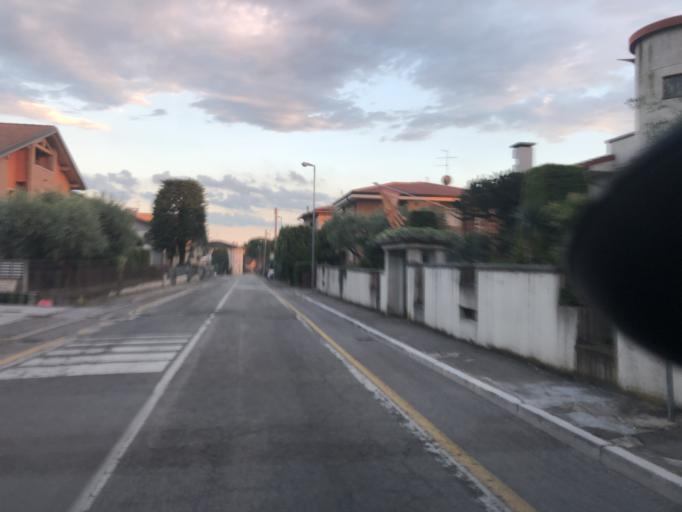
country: IT
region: Veneto
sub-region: Provincia di Verona
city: Settimo
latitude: 45.4793
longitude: 10.9034
